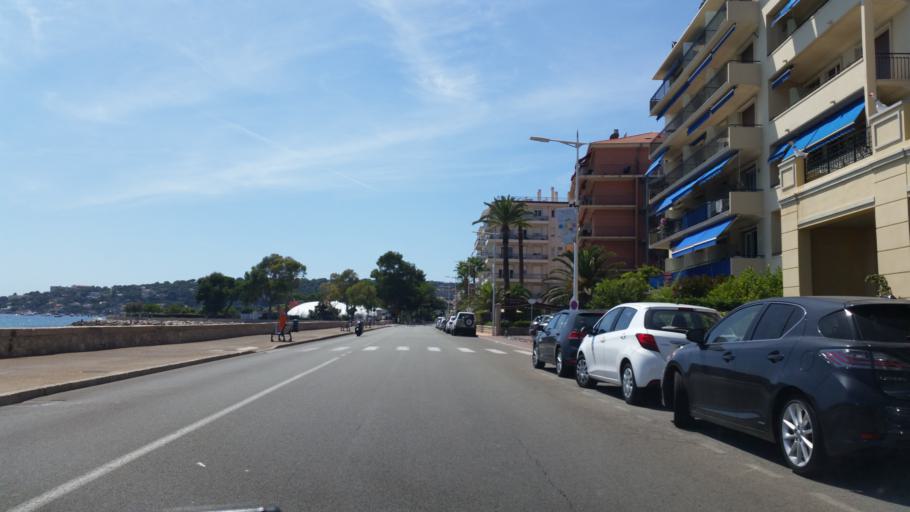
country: FR
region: Provence-Alpes-Cote d'Azur
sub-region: Departement des Alpes-Maritimes
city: Roquebrune-Cap-Martin
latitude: 43.7668
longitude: 7.4893
